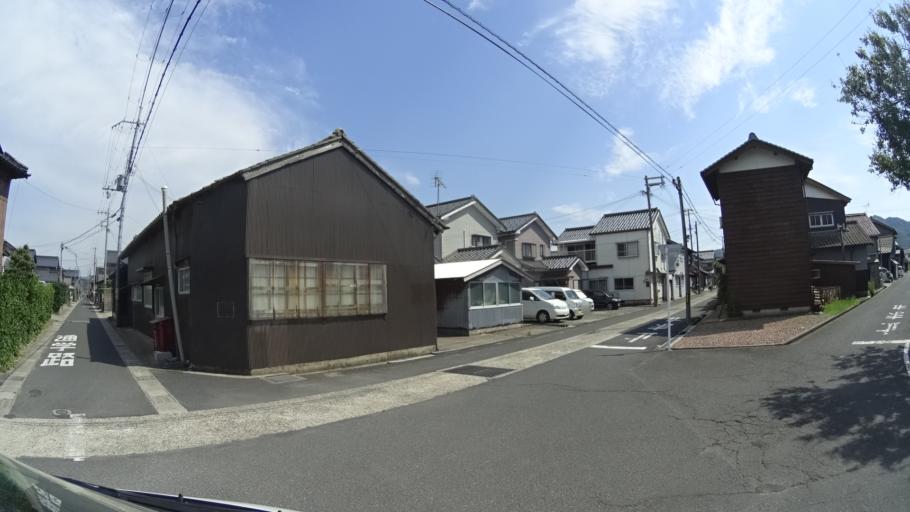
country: JP
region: Kyoto
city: Miyazu
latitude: 35.6887
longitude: 135.0296
